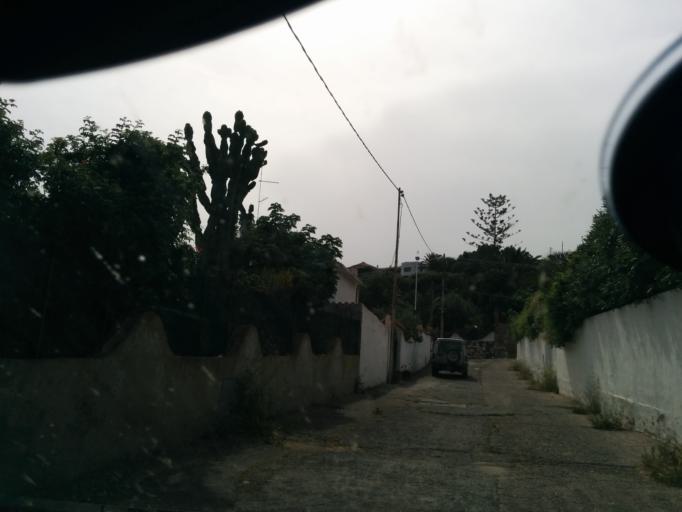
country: IT
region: Sardinia
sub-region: Provincia di Carbonia-Iglesias
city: Sant'Antioco
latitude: 38.9990
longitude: 8.4473
